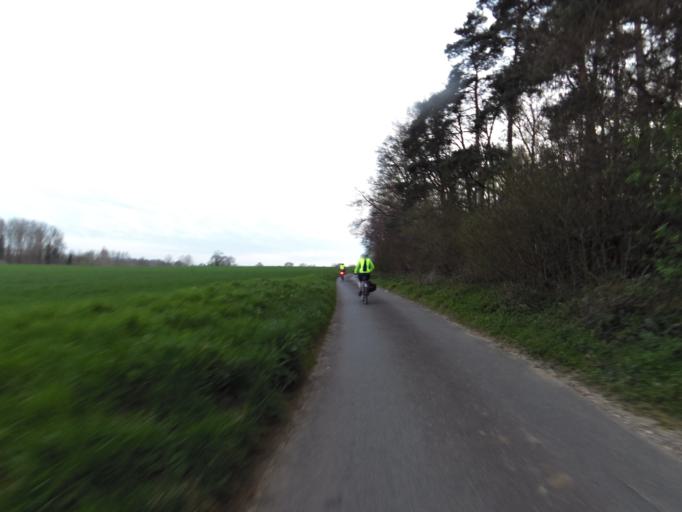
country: GB
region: England
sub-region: Suffolk
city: Kesgrave
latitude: 52.0985
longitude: 1.2470
